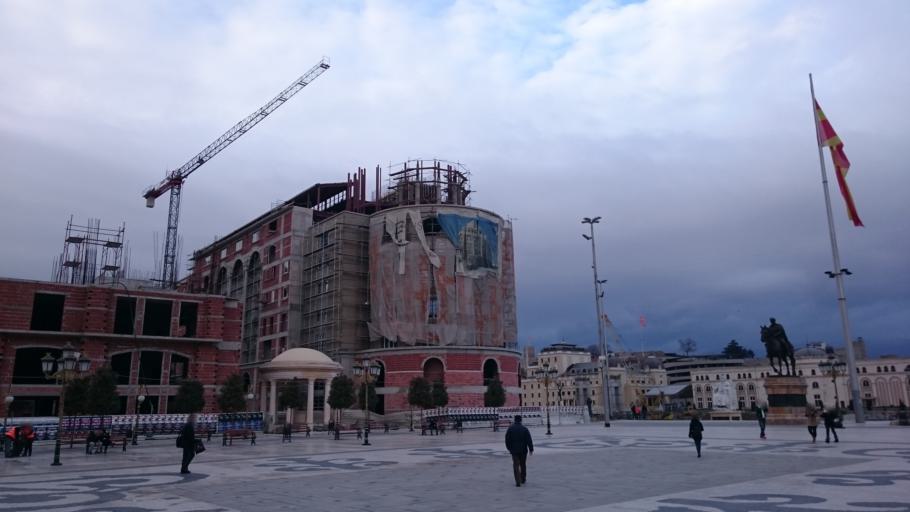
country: MK
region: Karpos
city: Skopje
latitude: 41.9960
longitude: 21.4319
